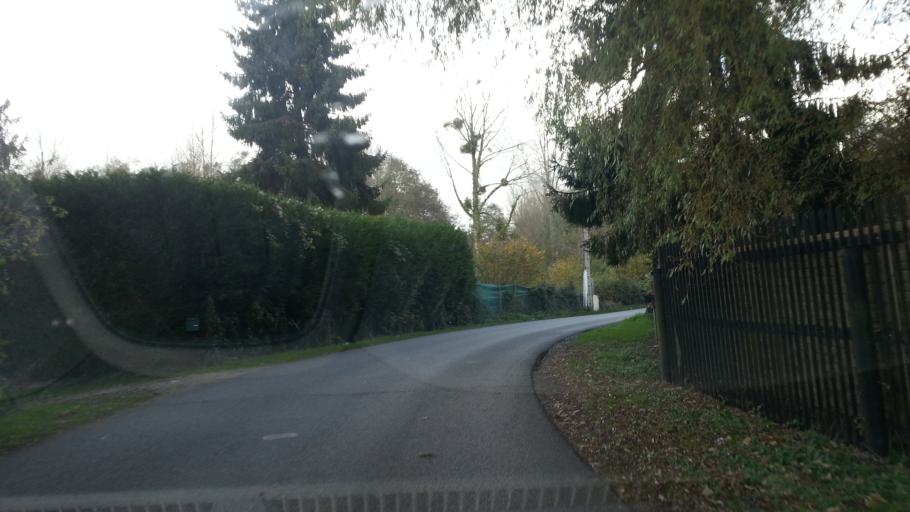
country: FR
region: Picardie
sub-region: Departement de l'Oise
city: Balagny-sur-Therain
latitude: 49.3016
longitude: 2.3425
